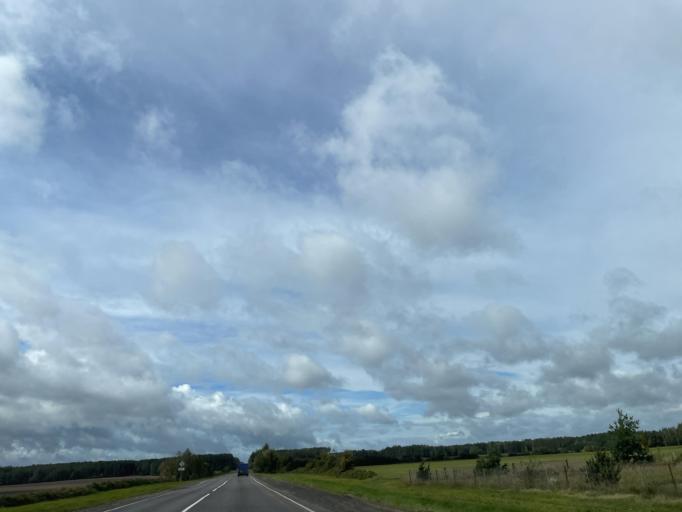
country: BY
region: Brest
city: Ivatsevichy
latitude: 52.7346
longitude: 25.2514
